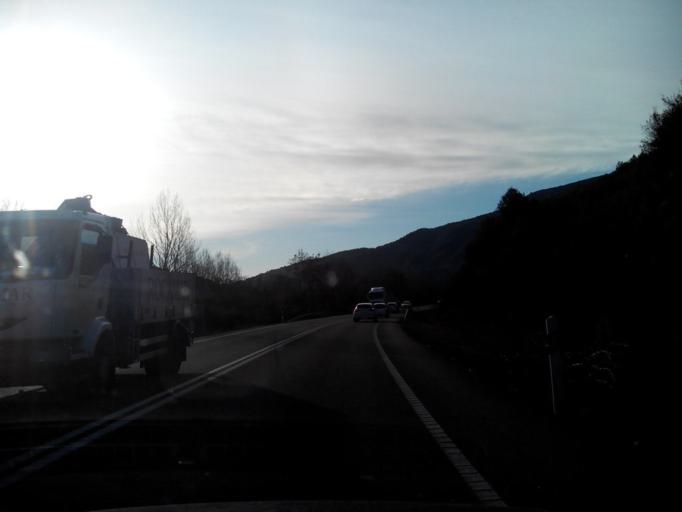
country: ES
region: Catalonia
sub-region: Provincia de Barcelona
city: Collbato
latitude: 41.5813
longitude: 1.8587
